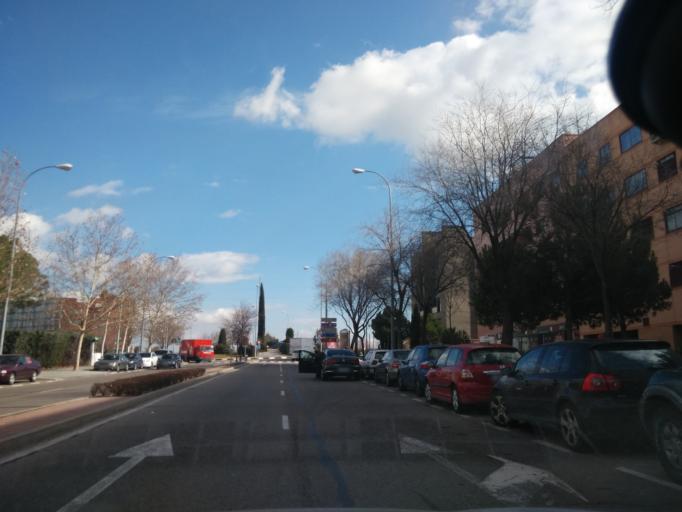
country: ES
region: Madrid
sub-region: Provincia de Madrid
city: Alcobendas
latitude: 40.5464
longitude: -3.6521
